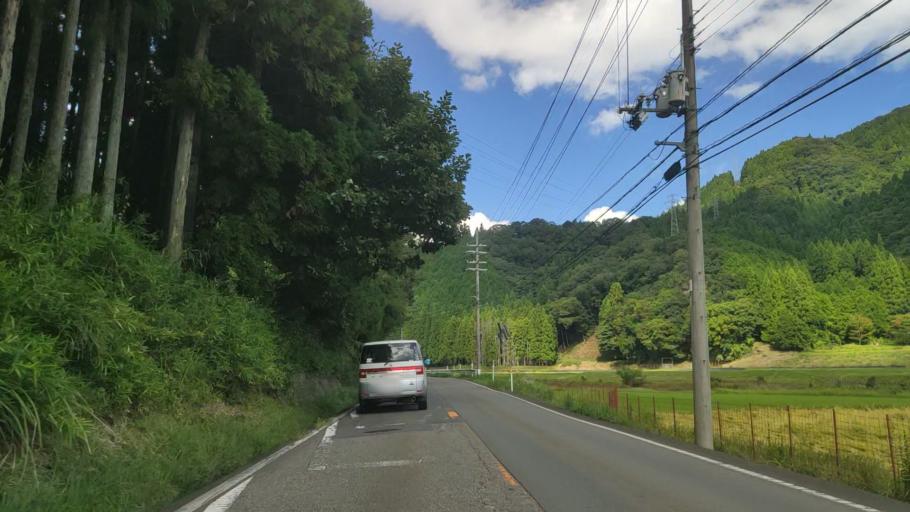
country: JP
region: Hyogo
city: Toyooka
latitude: 35.4807
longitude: 134.9523
